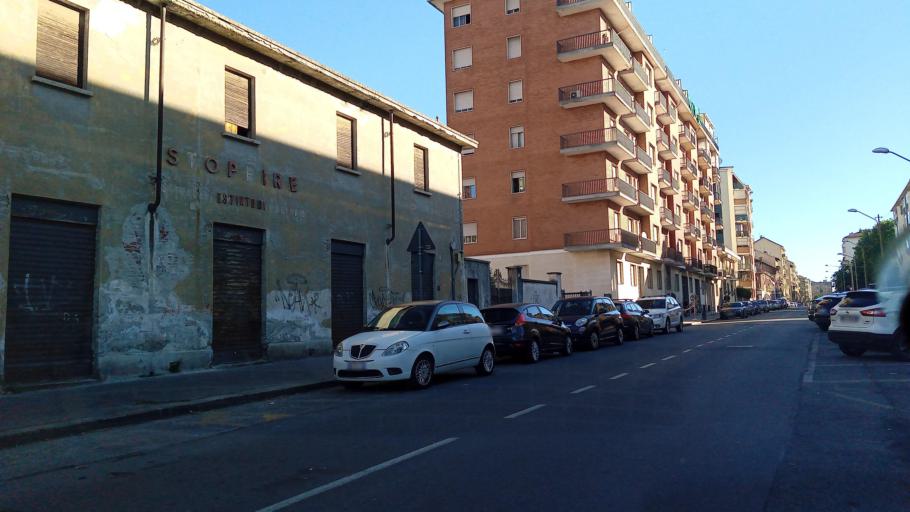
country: IT
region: Piedmont
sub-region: Provincia di Torino
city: Turin
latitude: 45.0937
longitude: 7.6587
